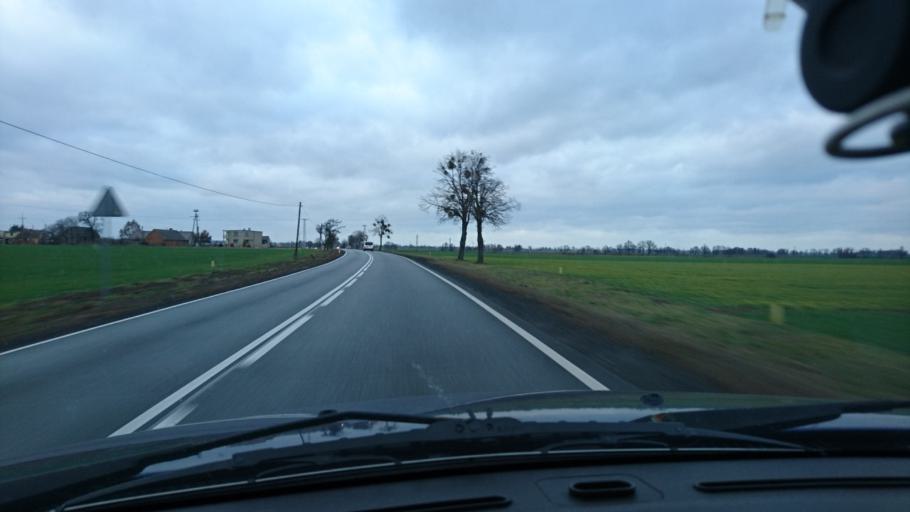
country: PL
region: Opole Voivodeship
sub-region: Powiat kluczborski
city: Kluczbork
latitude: 51.0099
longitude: 18.2040
